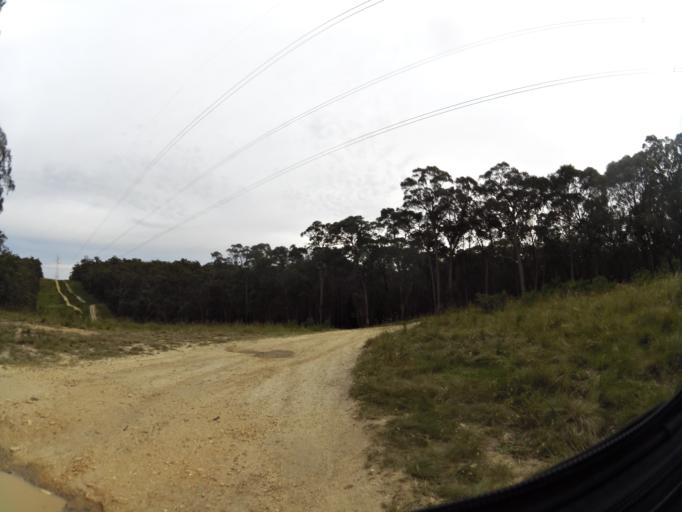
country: AU
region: Victoria
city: Brown Hill
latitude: -37.5292
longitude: 143.9047
